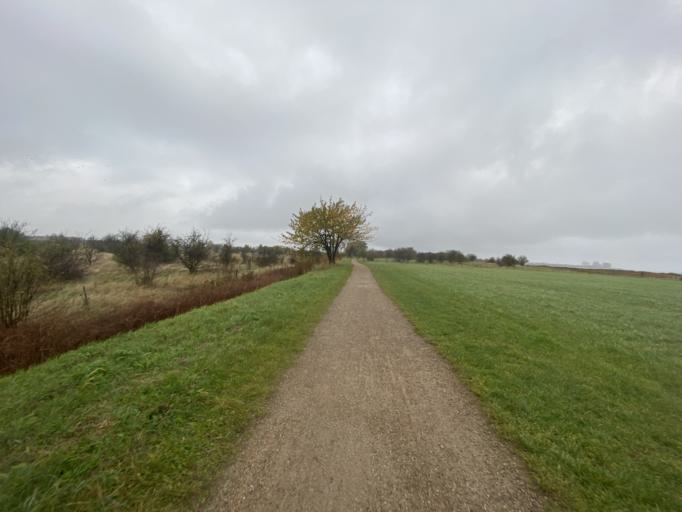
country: DK
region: Capital Region
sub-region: Dragor Kommune
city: Dragor
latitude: 55.5723
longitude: 12.6241
